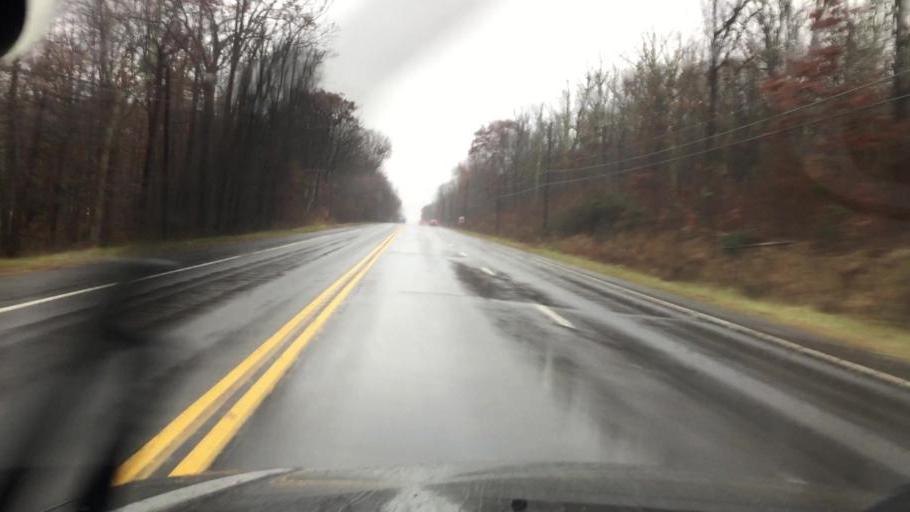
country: US
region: Pennsylvania
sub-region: Luzerne County
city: Freeland
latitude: 41.0975
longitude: -75.9316
